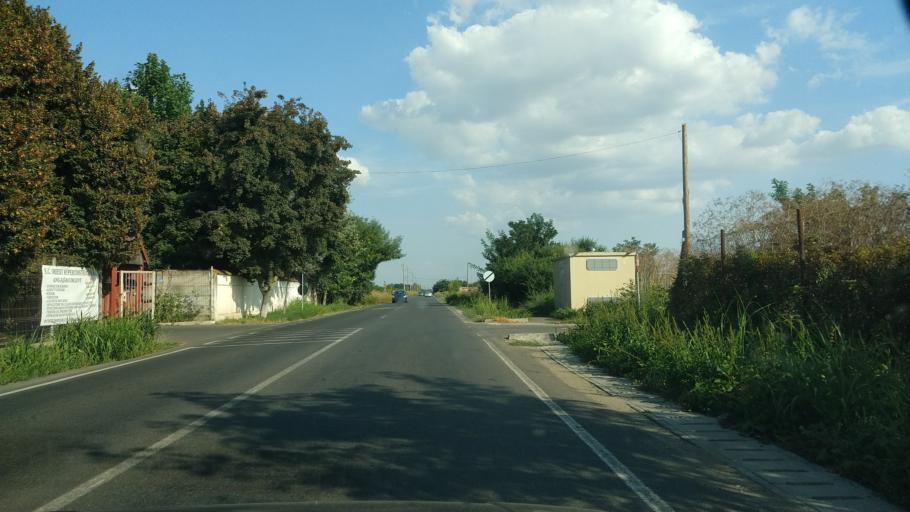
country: RO
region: Ilfov
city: Stefanestii de Jos
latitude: 44.5374
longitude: 26.2214
